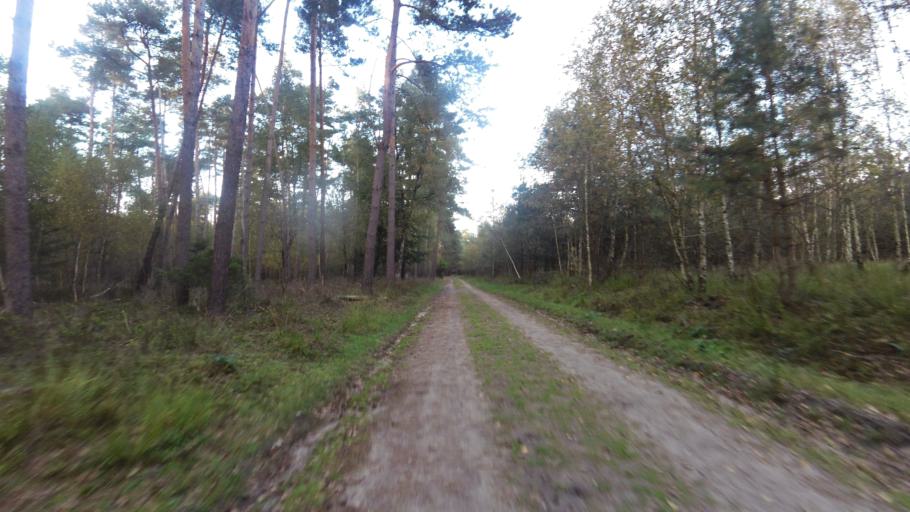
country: NL
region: Gelderland
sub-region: Gemeente Nunspeet
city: Nunspeet
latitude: 52.3219
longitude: 5.8402
